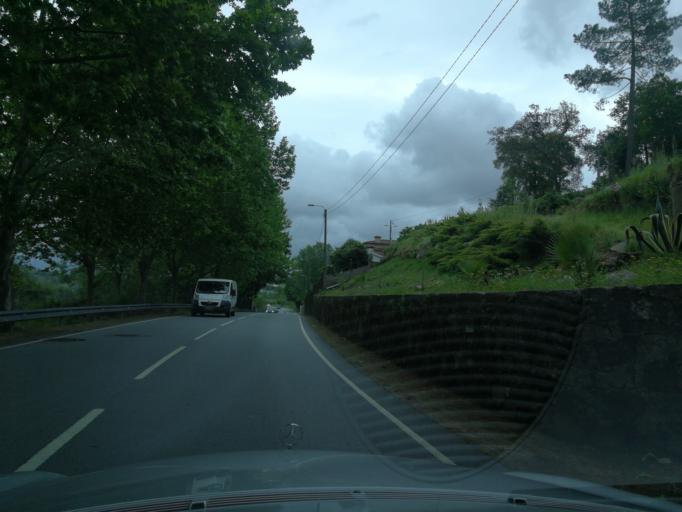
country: PT
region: Braga
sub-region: Braga
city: Adaufe
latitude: 41.6035
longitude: -8.4225
